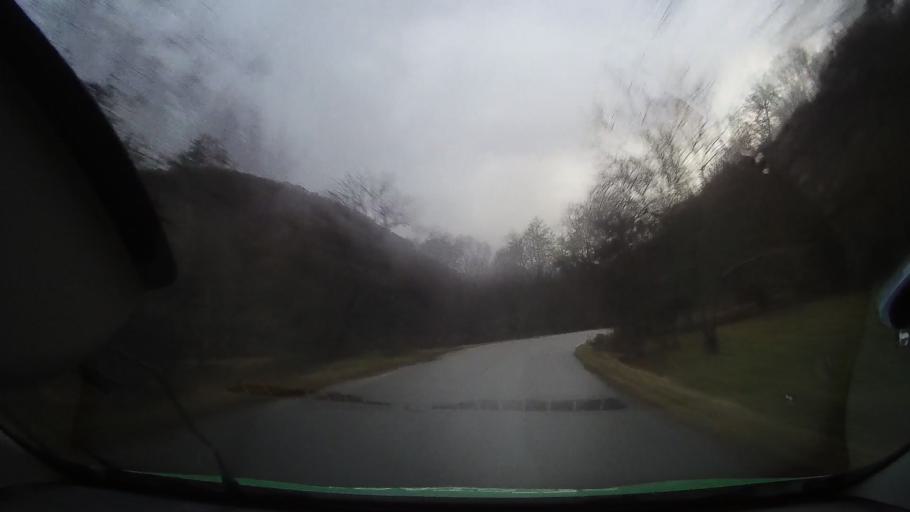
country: RO
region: Hunedoara
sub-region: Comuna Ribita
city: Ribita
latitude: 46.2704
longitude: 22.7428
